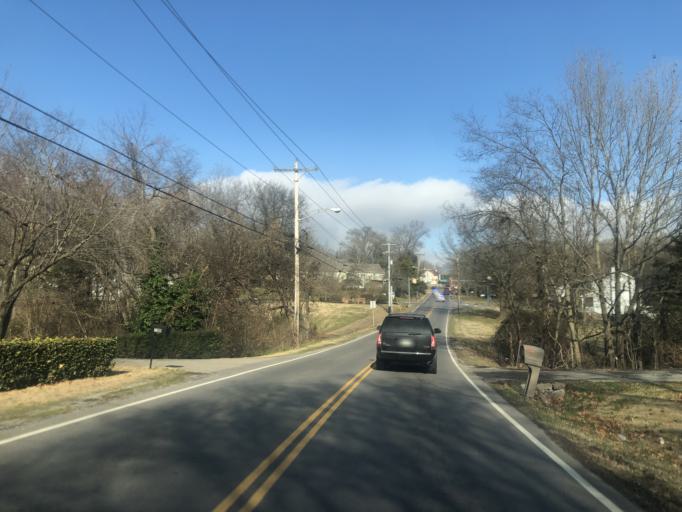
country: US
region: Tennessee
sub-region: Rutherford County
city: La Vergne
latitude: 36.0729
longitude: -86.6641
